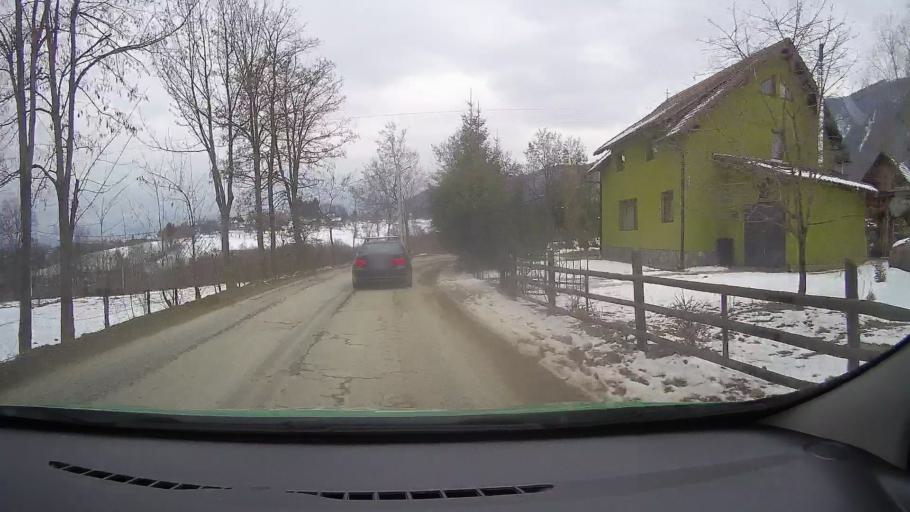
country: RO
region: Brasov
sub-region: Comuna Bran
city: Bran
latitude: 45.5364
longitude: 25.3400
